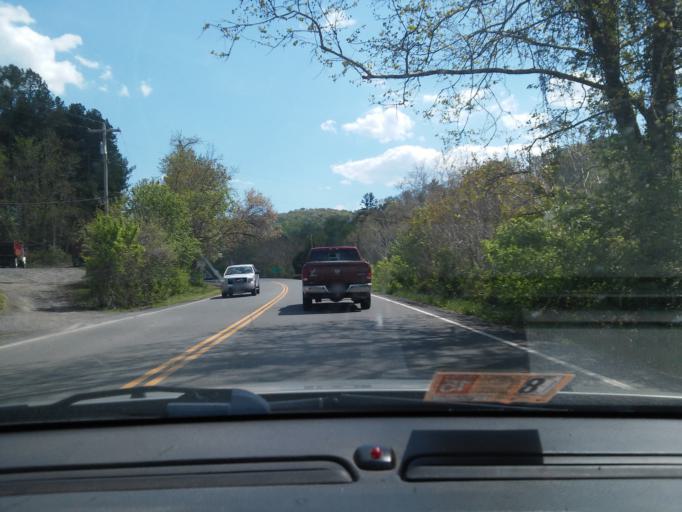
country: US
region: Virginia
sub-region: Warren County
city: Front Royal
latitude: 38.9052
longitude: -78.1850
